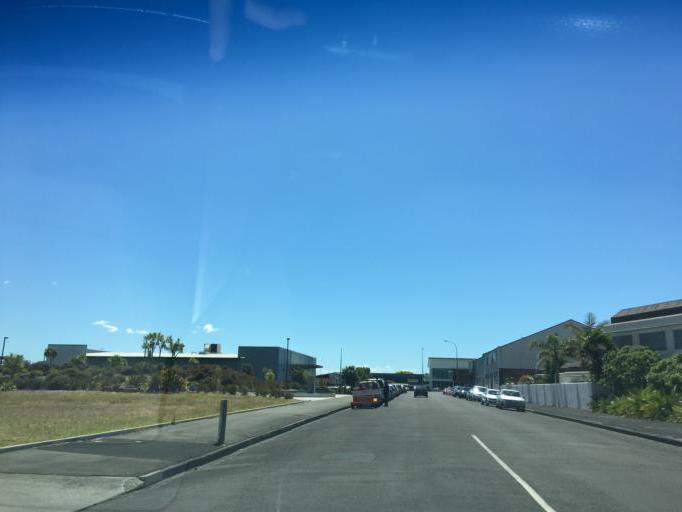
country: NZ
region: Gisborne
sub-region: Gisborne District
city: Gisborne
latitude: -38.6707
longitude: 178.0274
